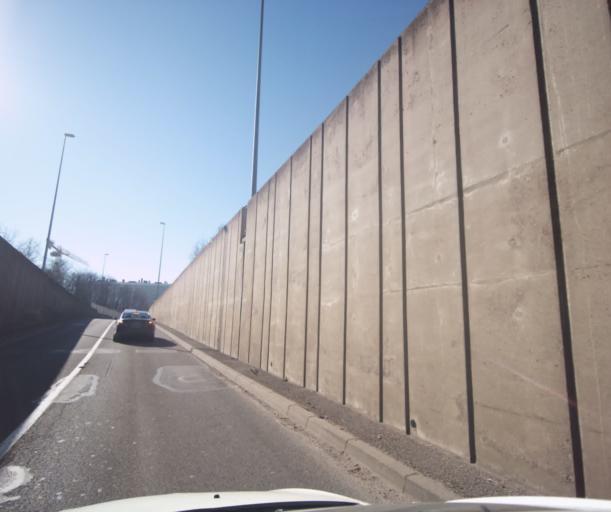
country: FR
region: Franche-Comte
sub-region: Departement du Doubs
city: Besancon
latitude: 47.2534
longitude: 6.0156
